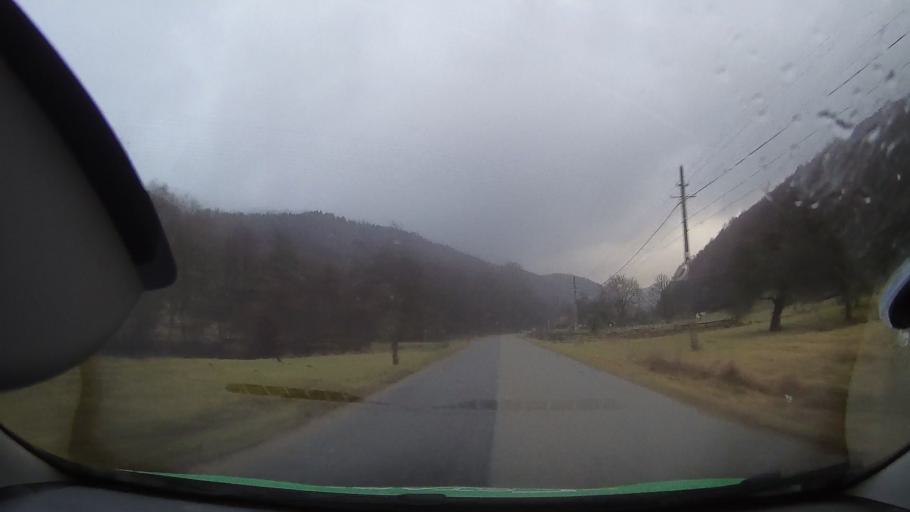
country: RO
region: Hunedoara
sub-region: Comuna Ribita
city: Ribita
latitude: 46.2592
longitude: 22.7452
